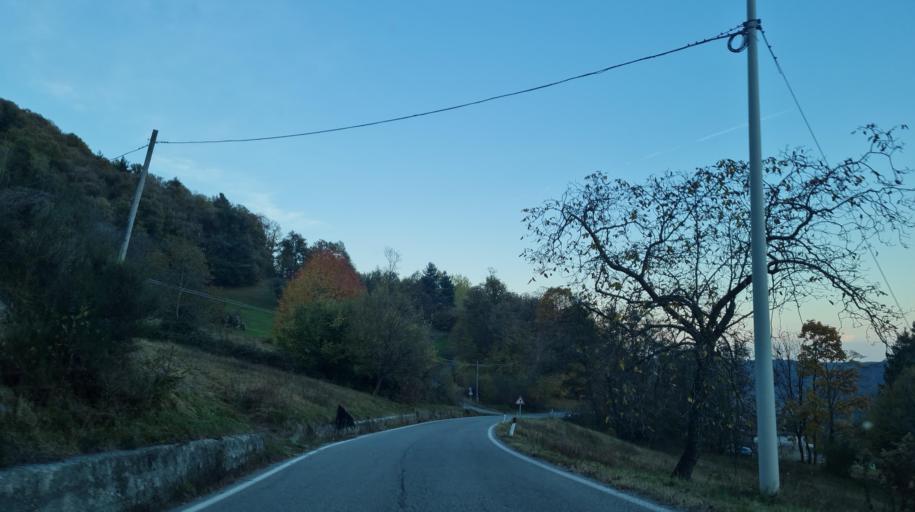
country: IT
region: Piedmont
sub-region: Provincia di Torino
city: Traversella
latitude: 45.5020
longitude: 7.7560
